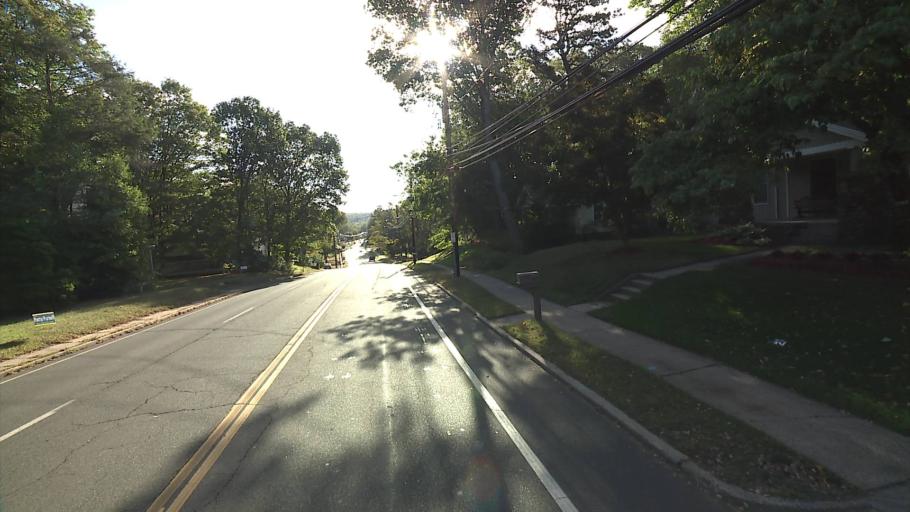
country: US
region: Connecticut
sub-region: New Haven County
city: Wallingford
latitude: 41.4923
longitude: -72.8265
